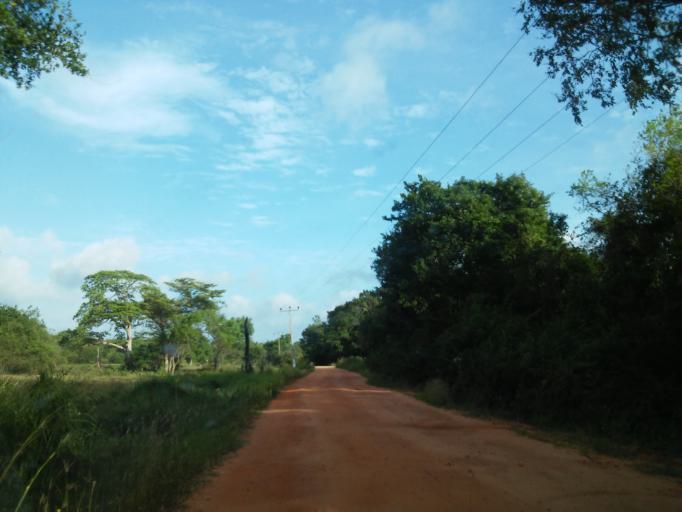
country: LK
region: Central
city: Sigiriya
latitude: 8.1711
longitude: 80.6814
